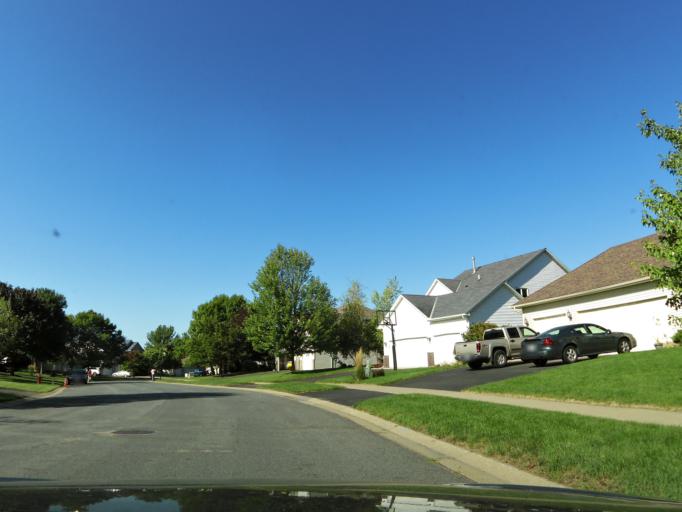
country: US
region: Minnesota
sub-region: Scott County
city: Savage
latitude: 44.7337
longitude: -93.3494
